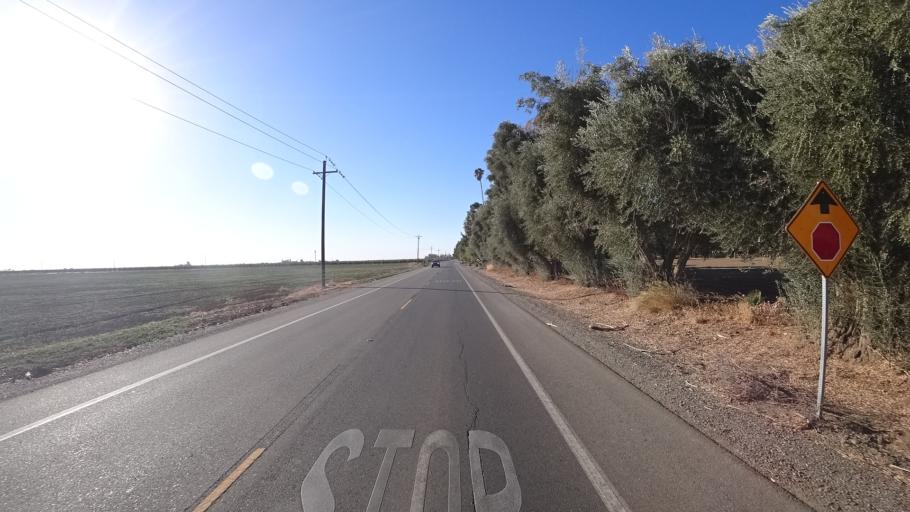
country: US
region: California
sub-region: Yolo County
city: Woodland
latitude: 38.6432
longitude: -121.7846
